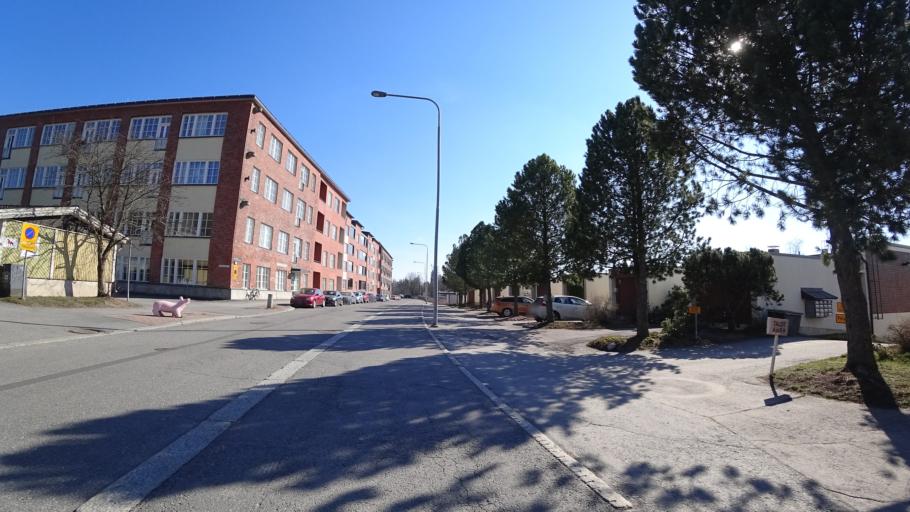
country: FI
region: Pirkanmaa
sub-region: Tampere
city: Pirkkala
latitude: 61.5097
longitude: 23.6625
